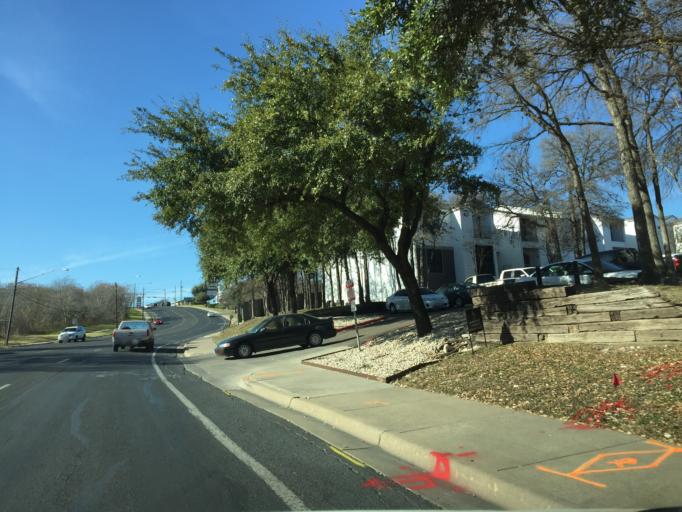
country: US
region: Texas
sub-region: Travis County
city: Austin
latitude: 30.2281
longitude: -97.7288
